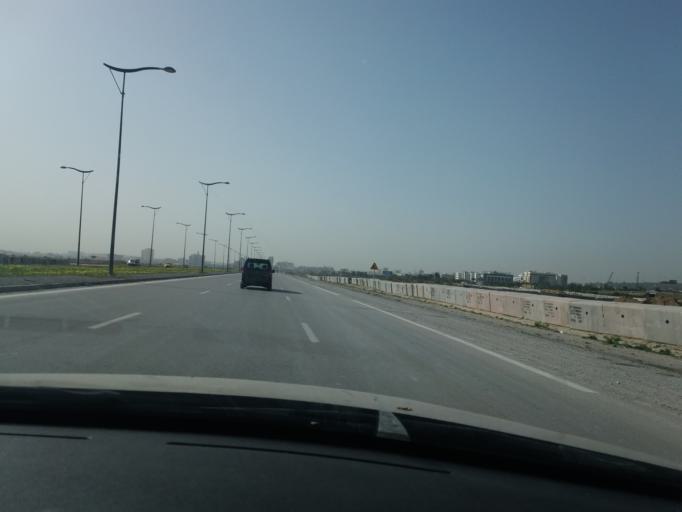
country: TN
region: Ariana
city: Ariana
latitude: 36.8249
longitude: 10.2056
